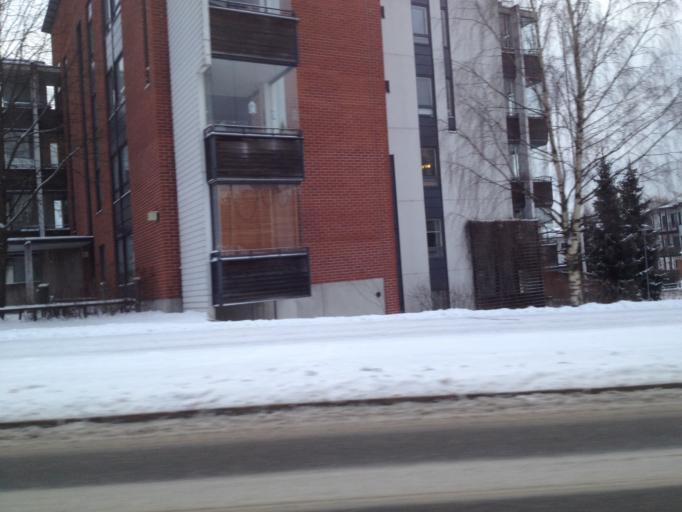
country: FI
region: Uusimaa
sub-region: Helsinki
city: Vantaa
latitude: 60.2177
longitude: 25.1470
